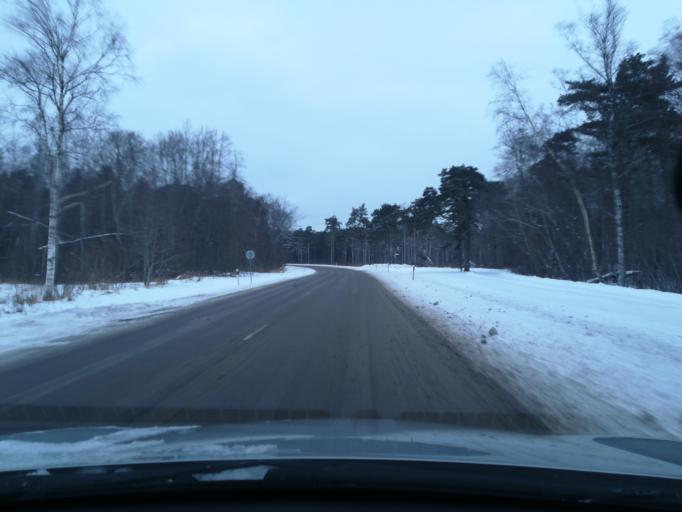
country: EE
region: Harju
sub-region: Keila linn
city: Keila
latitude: 59.4009
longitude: 24.3019
